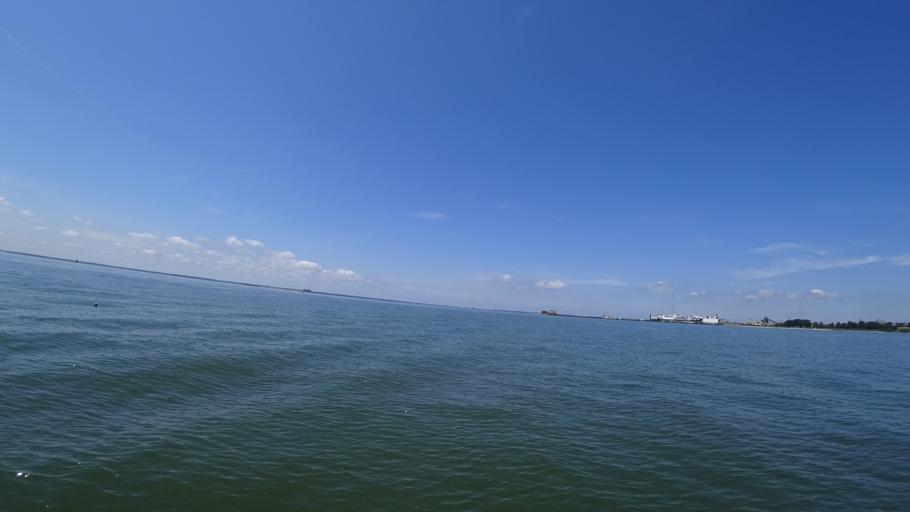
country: US
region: Virginia
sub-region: City of Newport News
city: Newport News
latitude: 36.9670
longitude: -76.3976
